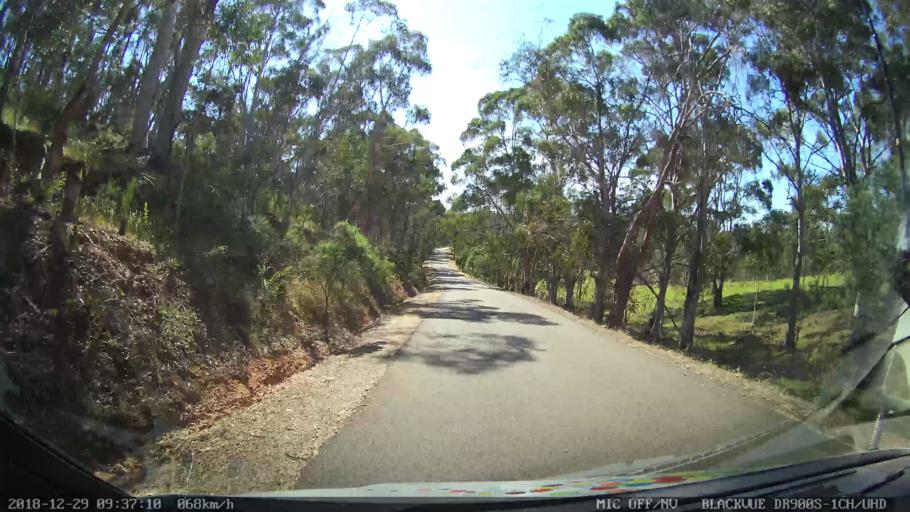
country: AU
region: New South Wales
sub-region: Upper Lachlan Shire
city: Crookwell
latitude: -34.6380
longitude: 149.3714
